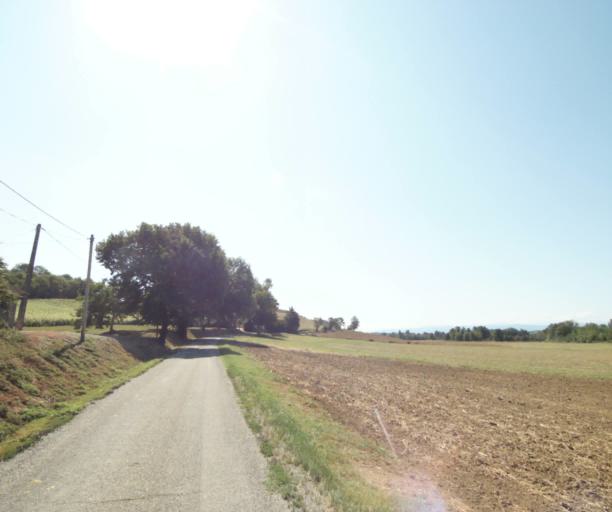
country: FR
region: Midi-Pyrenees
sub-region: Departement de l'Ariege
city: Lezat-sur-Leze
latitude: 43.2609
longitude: 1.3655
